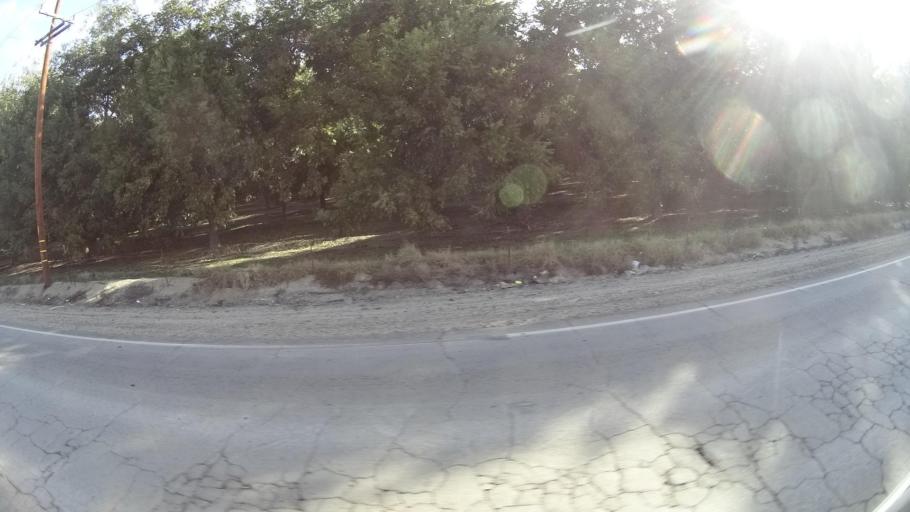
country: US
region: California
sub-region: Kern County
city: McFarland
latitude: 35.6239
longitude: -119.2044
